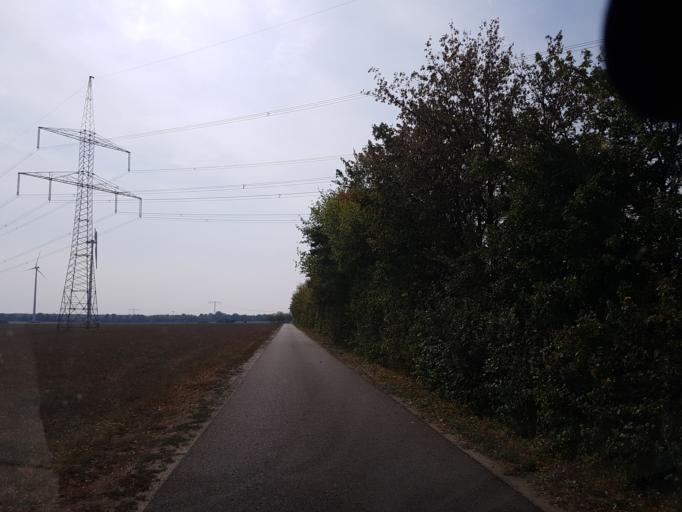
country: DE
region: Brandenburg
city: Finsterwalde
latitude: 51.6556
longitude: 13.7206
